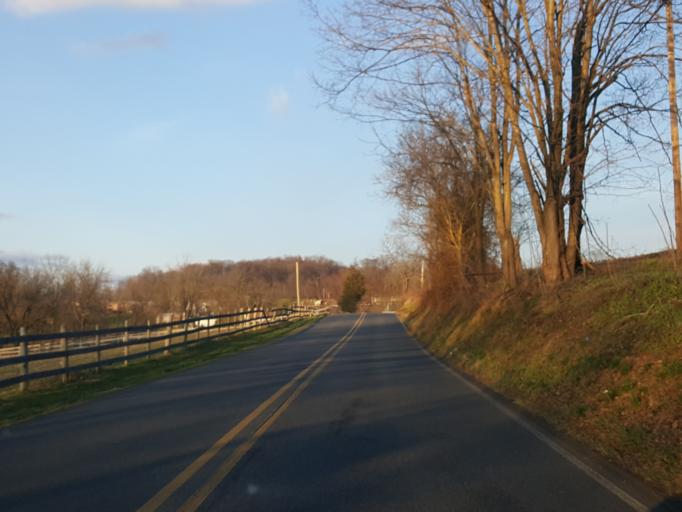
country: US
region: Pennsylvania
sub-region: Lebanon County
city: Jonestown
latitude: 40.3994
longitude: -76.4816
